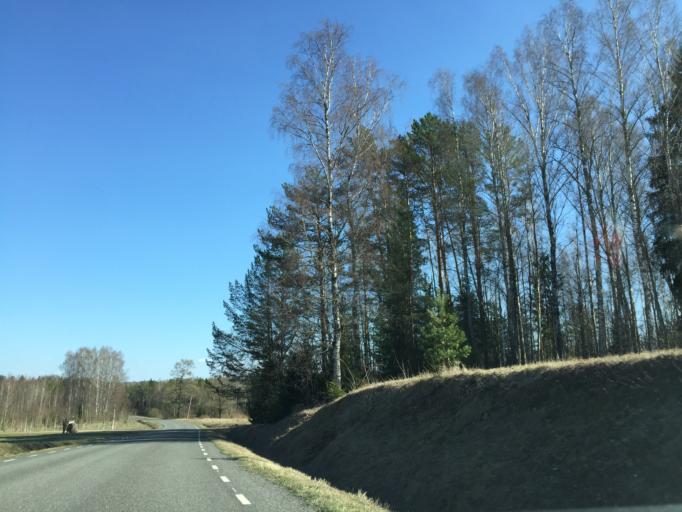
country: EE
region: Viljandimaa
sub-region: Viiratsi vald
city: Viiratsi
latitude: 58.2707
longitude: 25.6429
